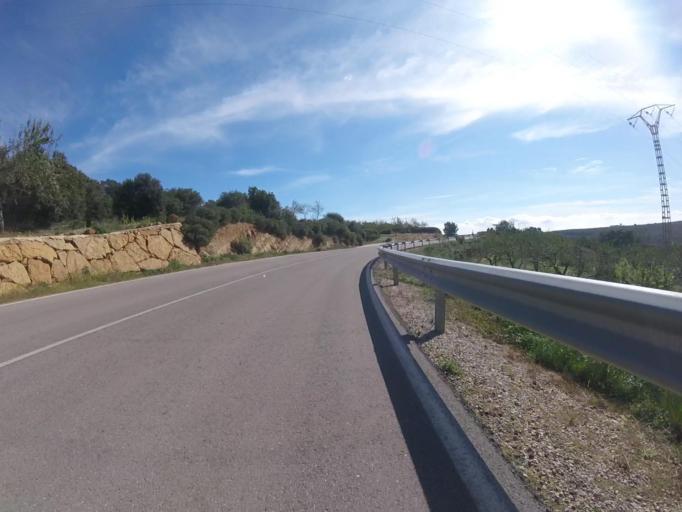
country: ES
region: Valencia
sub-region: Provincia de Castello
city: Sarratella
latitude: 40.3062
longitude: 0.0317
